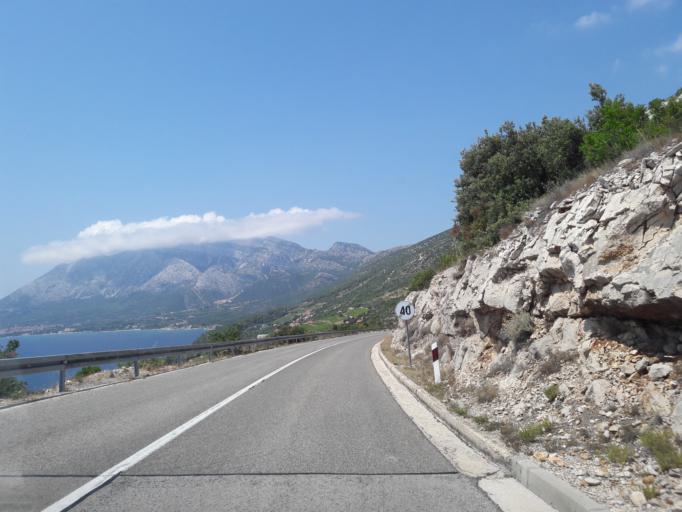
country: HR
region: Dubrovacko-Neretvanska
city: Orebic
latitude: 42.9704
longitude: 17.2428
